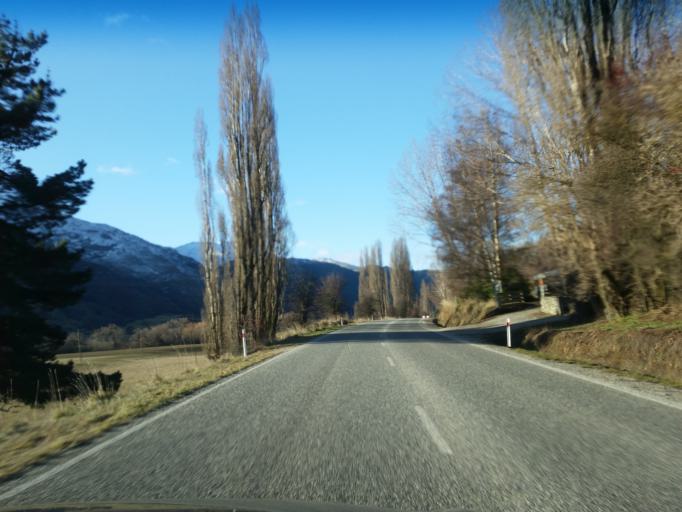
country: NZ
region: Otago
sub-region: Queenstown-Lakes District
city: Arrowtown
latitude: -44.9595
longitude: 168.7263
